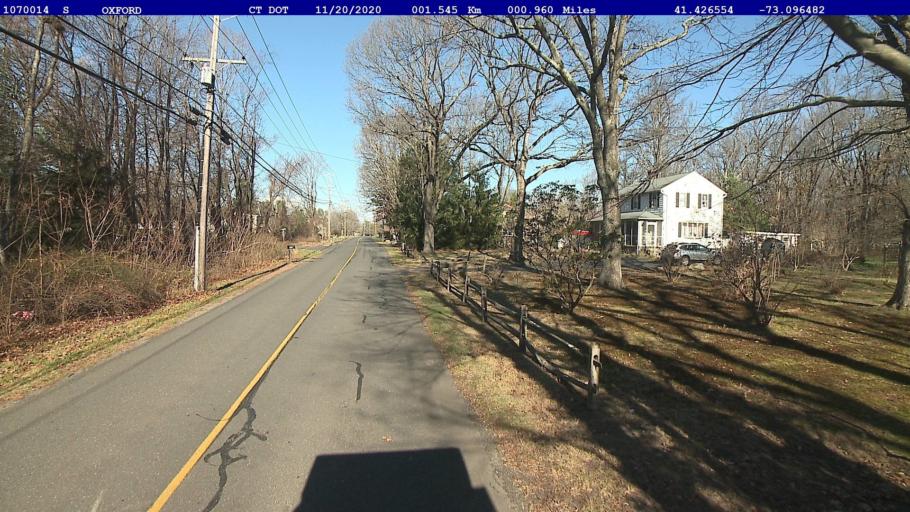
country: US
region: Connecticut
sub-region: New Haven County
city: Oxford
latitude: 41.4266
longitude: -73.0965
